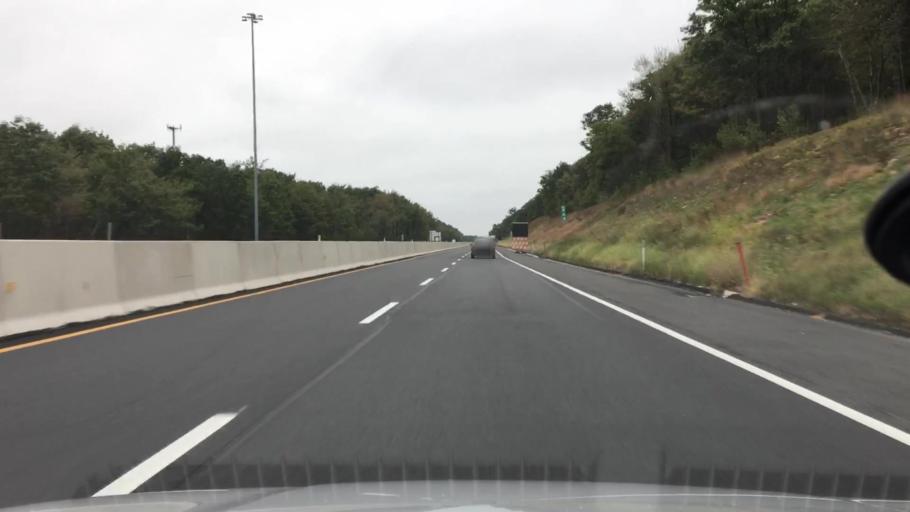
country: US
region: Pennsylvania
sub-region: Luzerne County
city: White Haven
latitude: 41.0742
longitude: -75.7091
